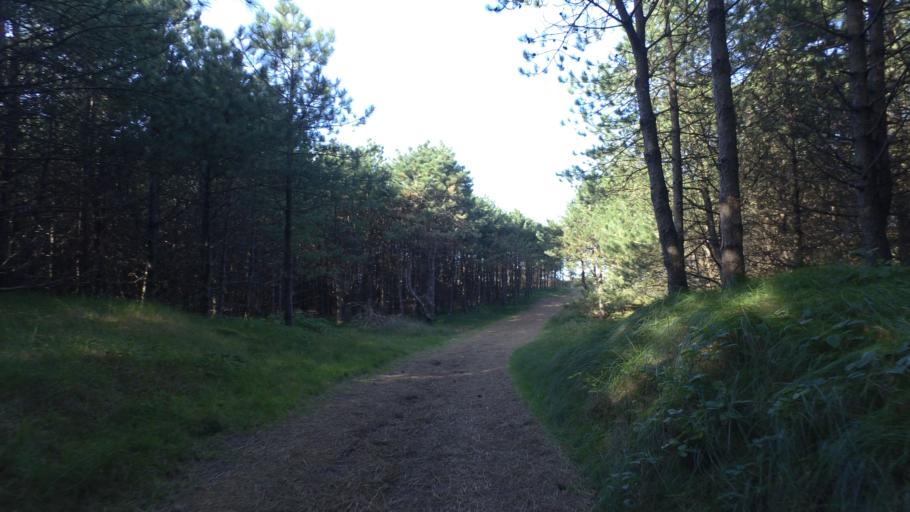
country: NL
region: Friesland
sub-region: Gemeente Ameland
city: Nes
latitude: 53.4580
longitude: 5.7827
